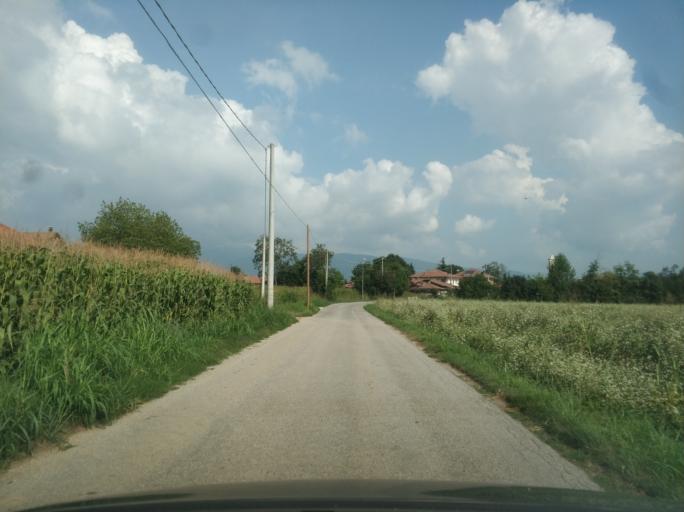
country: IT
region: Piedmont
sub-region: Provincia di Cuneo
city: Caraglio
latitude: 44.4349
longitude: 7.4314
